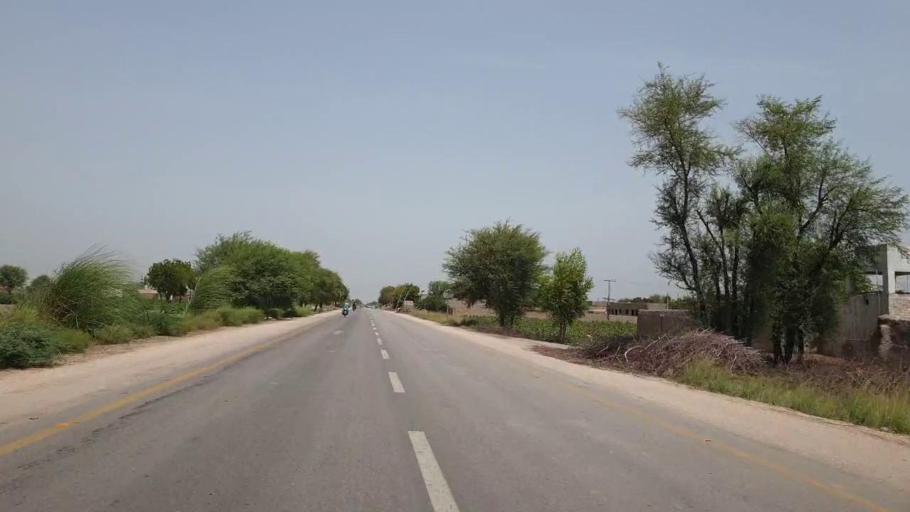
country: PK
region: Sindh
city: Shahpur Chakar
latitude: 26.1665
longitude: 68.6249
